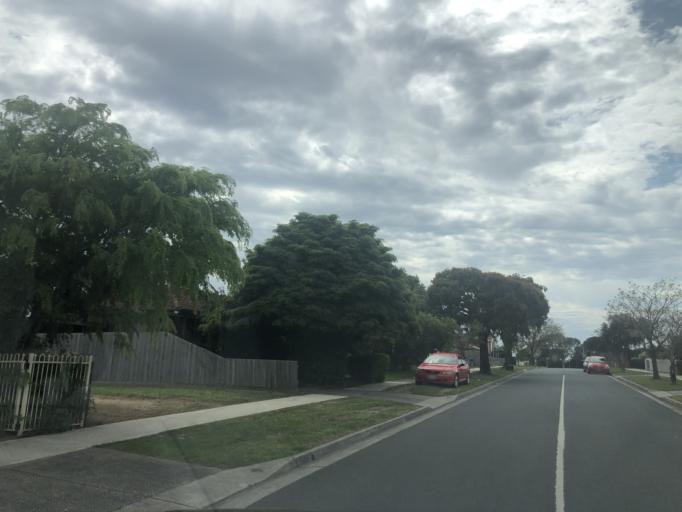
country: AU
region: Victoria
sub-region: Casey
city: Hallam
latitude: -38.0019
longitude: 145.2635
